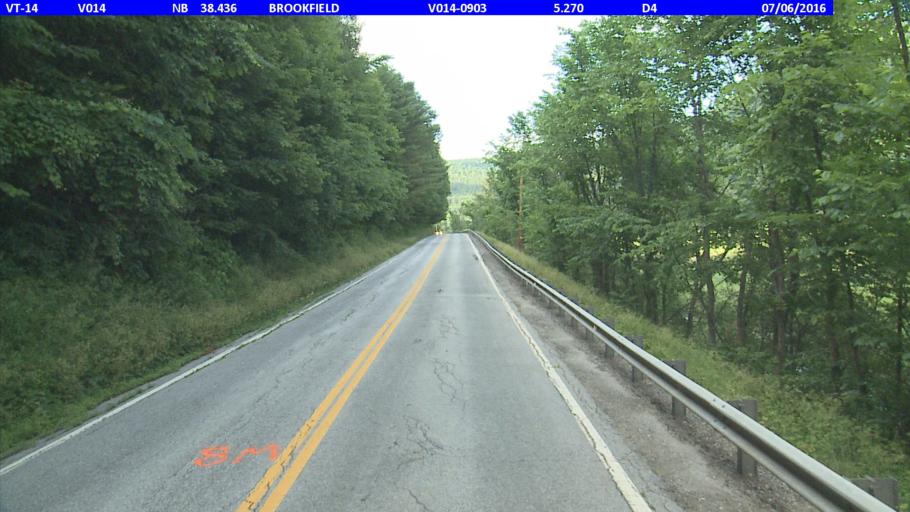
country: US
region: Vermont
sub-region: Orange County
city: Williamstown
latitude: 44.0523
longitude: -72.5636
